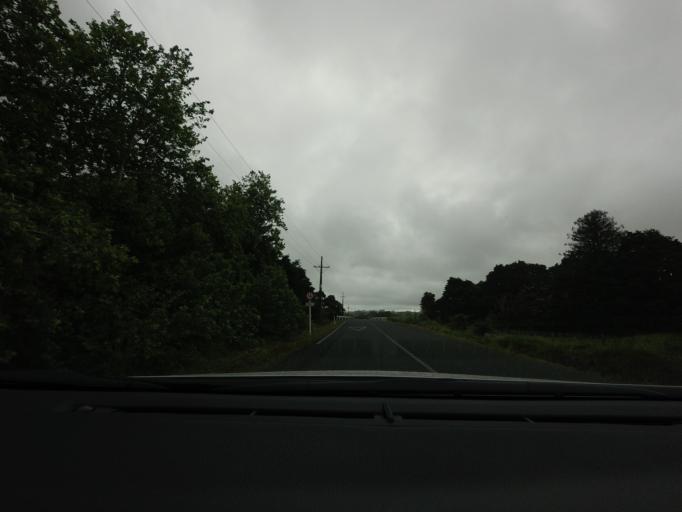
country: NZ
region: Auckland
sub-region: Auckland
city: Wellsford
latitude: -36.2813
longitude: 174.5778
